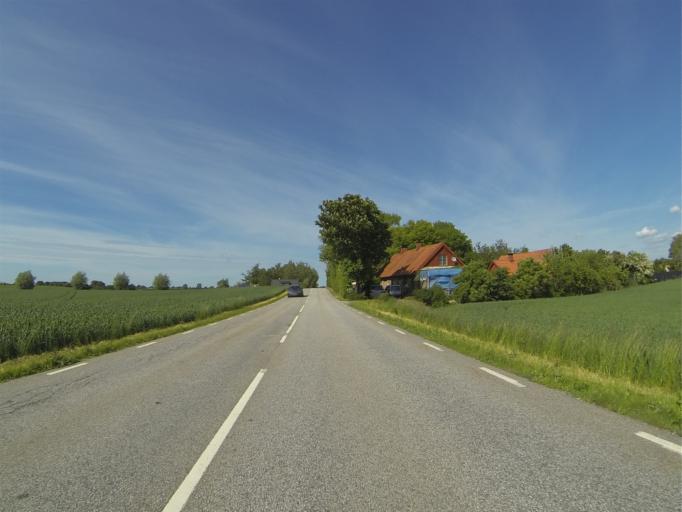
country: SE
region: Skane
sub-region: Staffanstorps Kommun
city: Hjaerup
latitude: 55.6354
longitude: 13.1165
